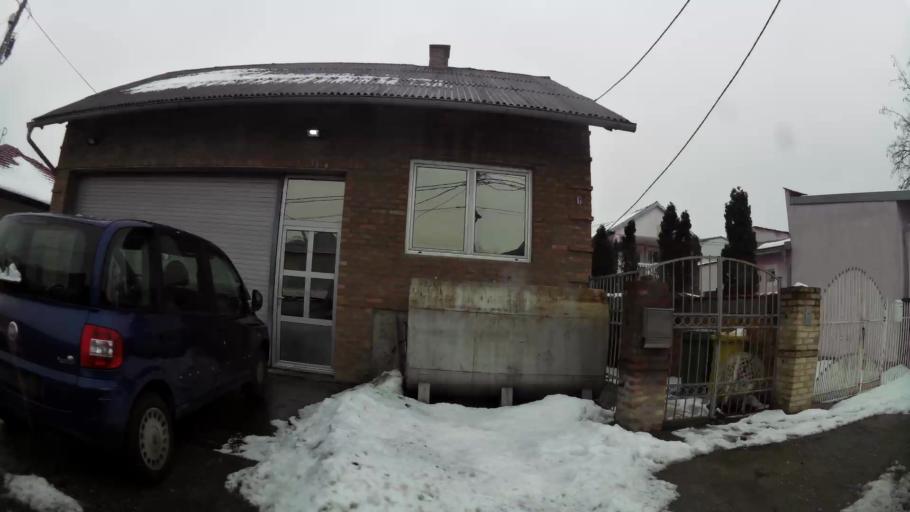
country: RS
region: Central Serbia
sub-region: Belgrade
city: Zemun
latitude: 44.8496
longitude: 20.3579
